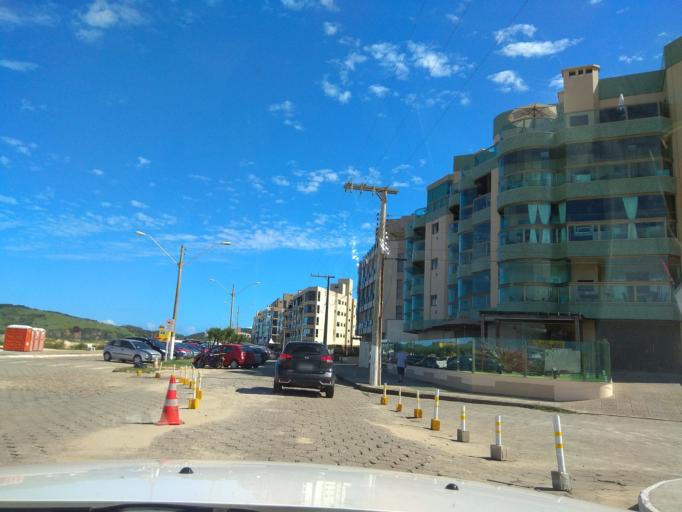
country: BR
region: Santa Catarina
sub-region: Laguna
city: Laguna
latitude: -28.4860
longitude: -48.7661
